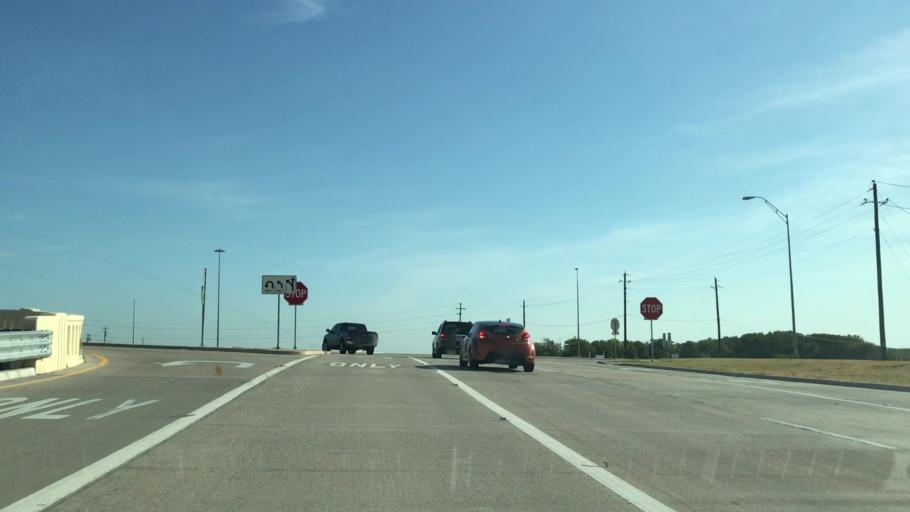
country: US
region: Texas
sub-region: Collin County
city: McKinney
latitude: 33.2392
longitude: -96.6296
